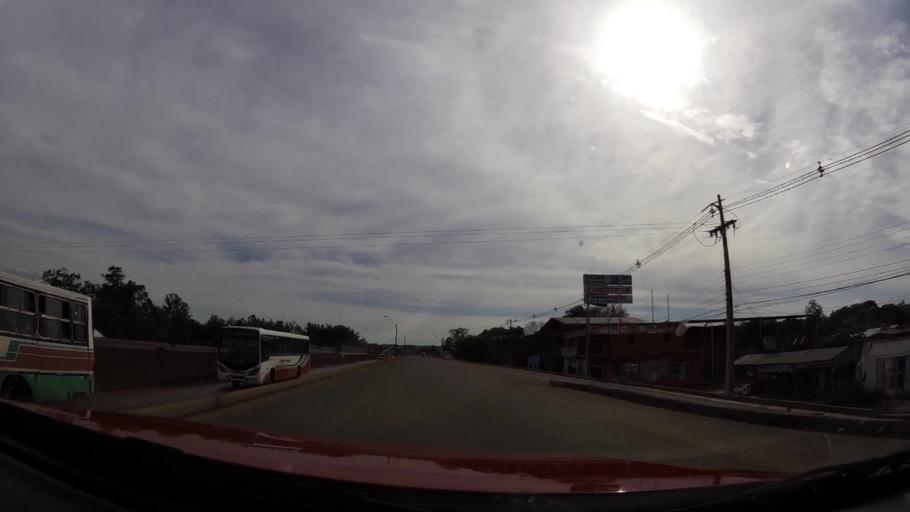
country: PY
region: Central
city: Limpio
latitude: -25.1810
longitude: -57.4904
